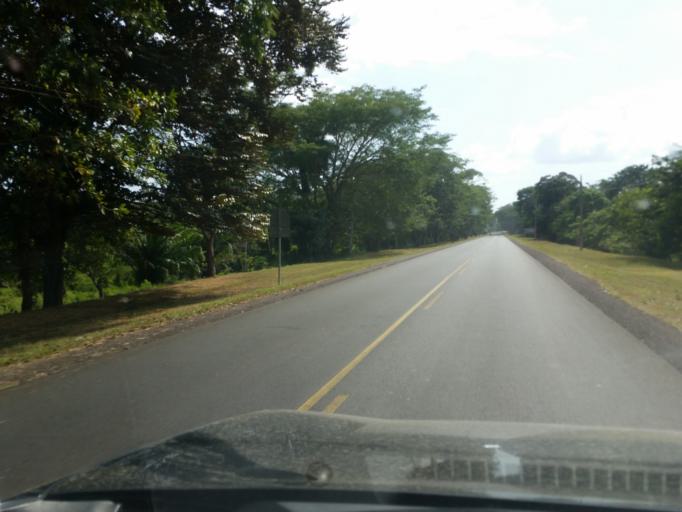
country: NI
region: Rio San Juan
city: San Miguelito
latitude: 11.5491
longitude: -84.8246
